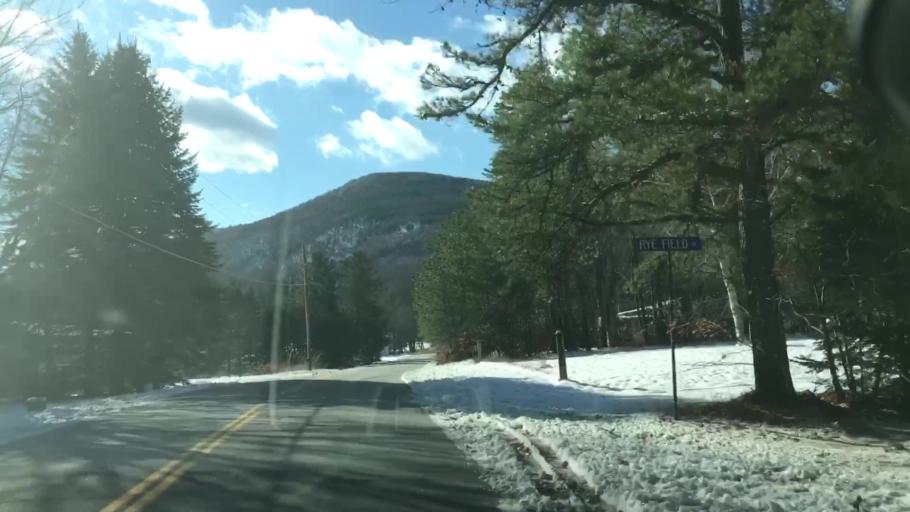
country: US
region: Maine
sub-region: Oxford County
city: Brownfield
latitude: 43.9371
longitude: -70.8919
